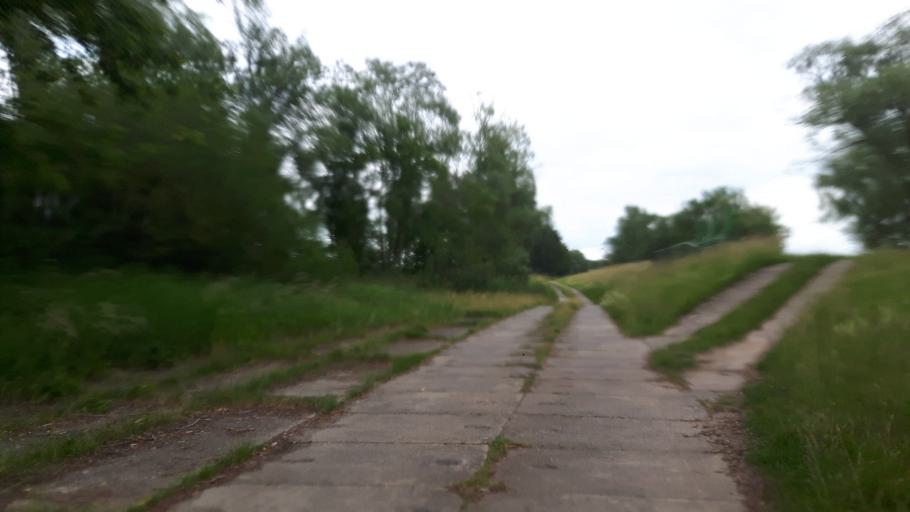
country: DE
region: Brandenburg
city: Schwedt (Oder)
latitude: 53.0764
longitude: 14.3389
